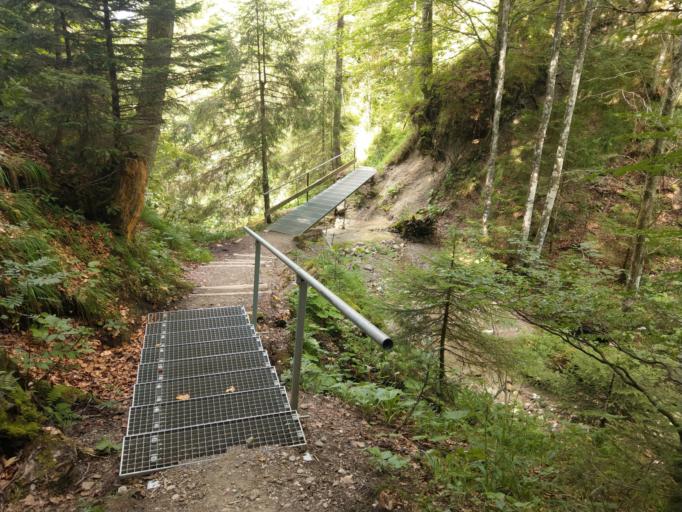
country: DE
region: Bavaria
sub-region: Swabia
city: Nesselwang
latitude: 47.6085
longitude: 10.5018
